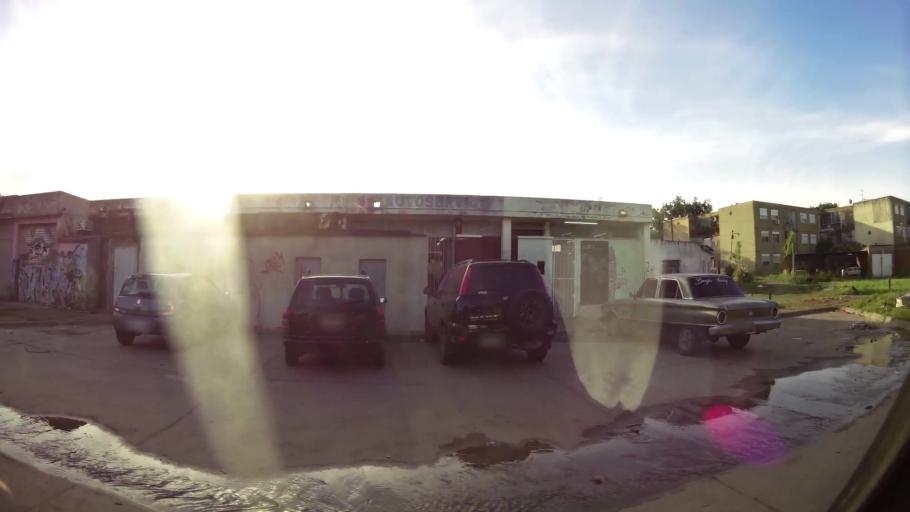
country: AR
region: Buenos Aires
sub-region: Partido de Almirante Brown
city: Adrogue
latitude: -34.8205
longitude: -58.3417
